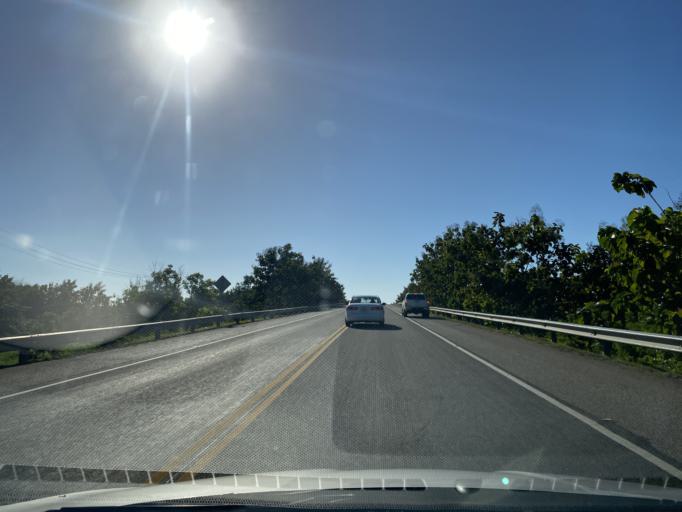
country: DO
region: Santo Domingo
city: Guerra
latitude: 18.5284
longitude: -69.7506
